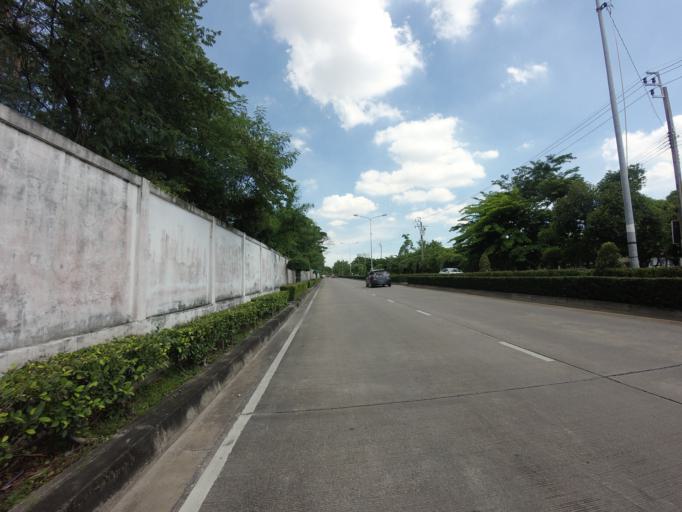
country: TH
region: Bangkok
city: Chatuchak
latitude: 13.8505
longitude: 100.5884
